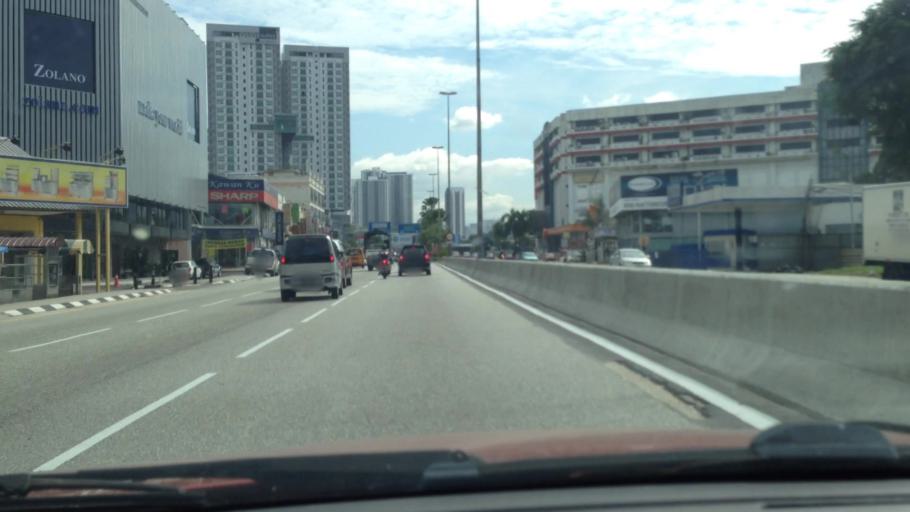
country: MY
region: Kuala Lumpur
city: Kuala Lumpur
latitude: 3.0884
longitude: 101.6741
